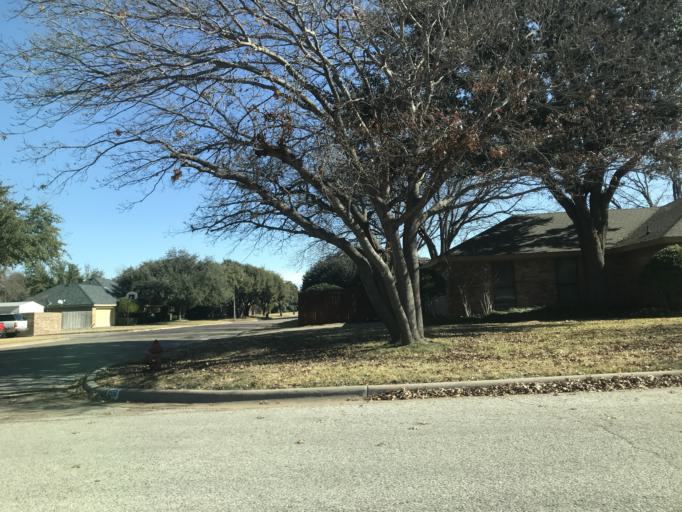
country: US
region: Texas
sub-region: Taylor County
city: Abilene
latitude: 32.3829
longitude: -99.7575
